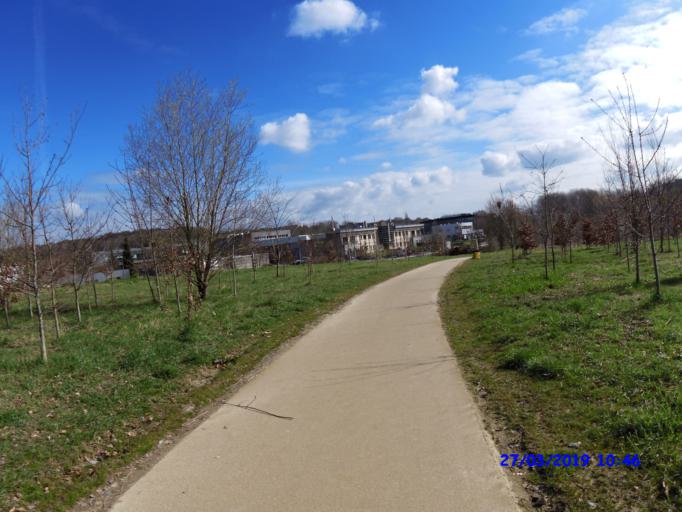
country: BE
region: Flanders
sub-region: Provincie Vlaams-Brabant
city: Wemmel
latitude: 50.8796
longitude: 4.2926
